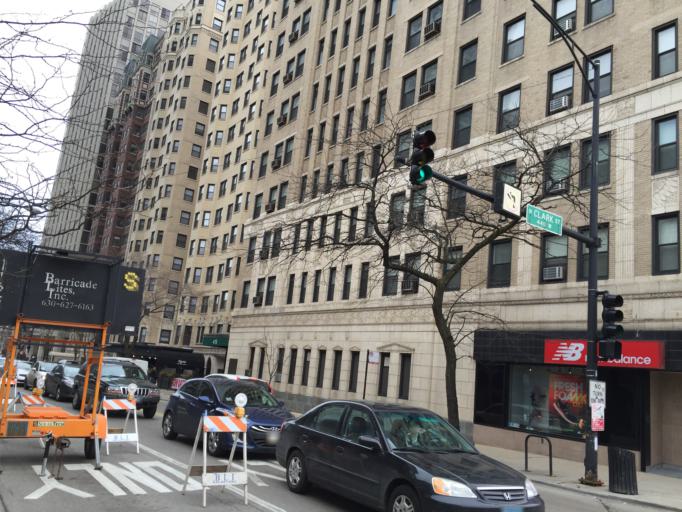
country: US
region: Illinois
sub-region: Cook County
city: Chicago
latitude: 41.9256
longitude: -87.6404
